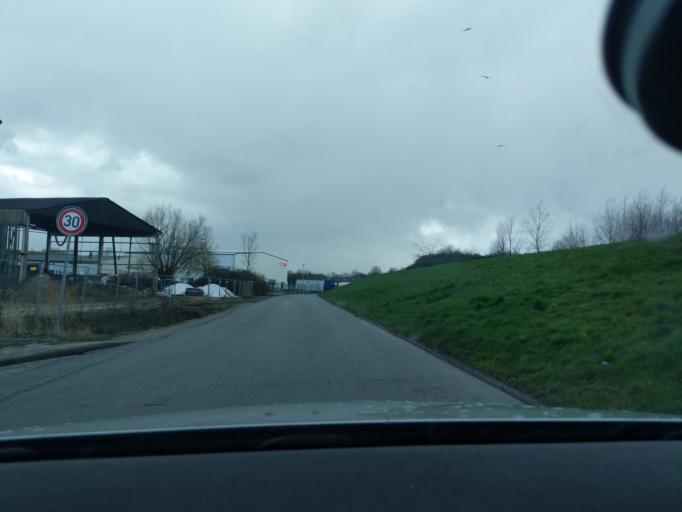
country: DE
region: Lower Saxony
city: Stade
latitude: 53.6067
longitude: 9.4870
